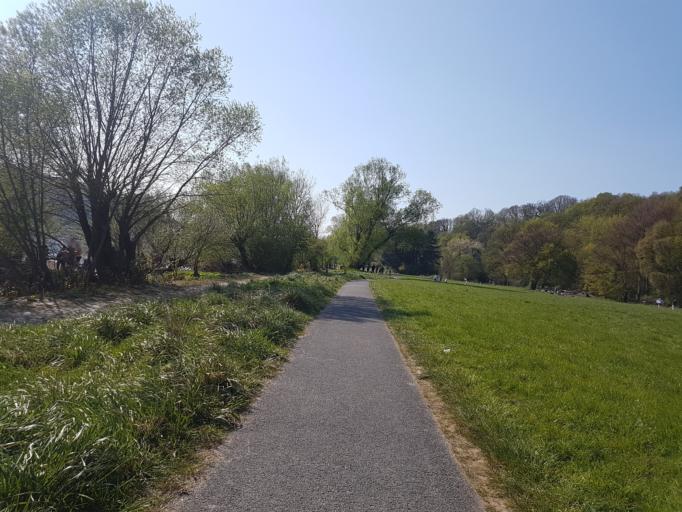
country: DE
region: North Rhine-Westphalia
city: Hattingen
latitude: 51.4121
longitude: 7.2446
